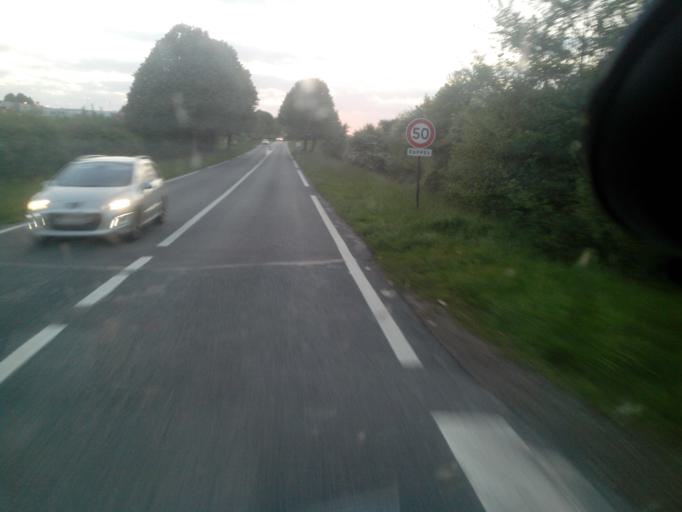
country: FR
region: Nord-Pas-de-Calais
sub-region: Departement du Pas-de-Calais
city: Hesdin
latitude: 50.3665
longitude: 2.0336
